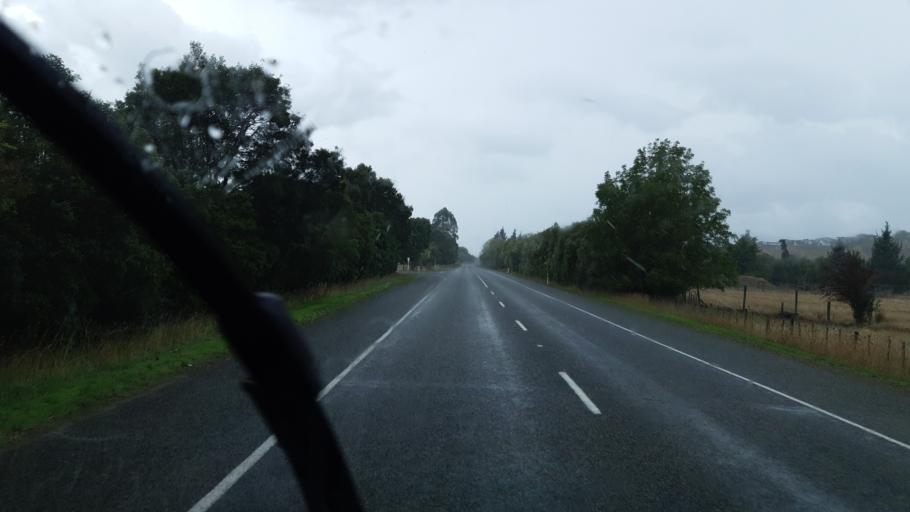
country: NZ
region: Tasman
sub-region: Tasman District
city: Brightwater
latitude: -41.3802
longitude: 173.0901
